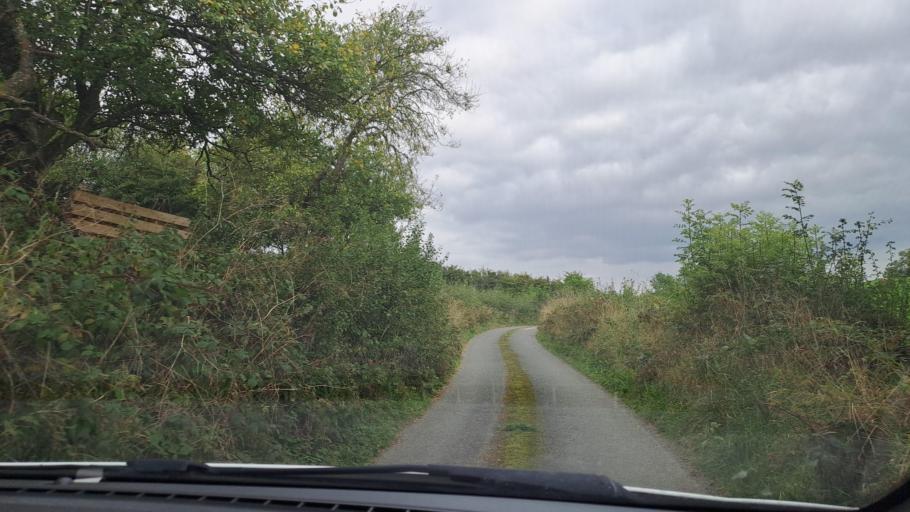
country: IE
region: Ulster
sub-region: An Cabhan
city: Kingscourt
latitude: 53.9767
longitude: -6.8539
